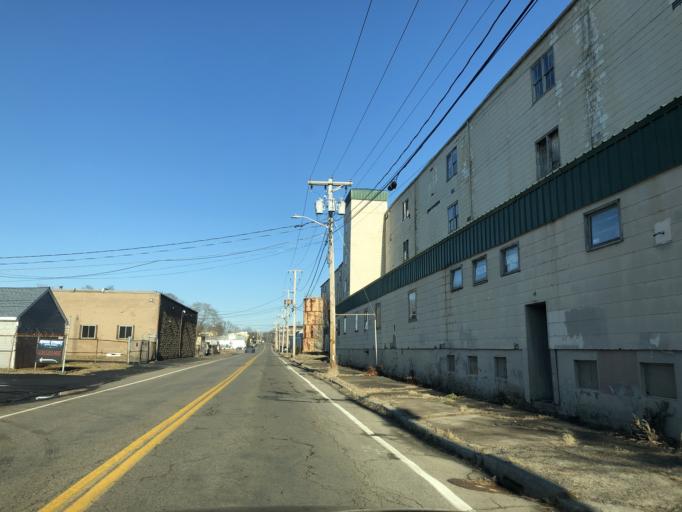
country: US
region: Massachusetts
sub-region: Plymouth County
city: Brockton
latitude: 42.1035
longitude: -71.0185
